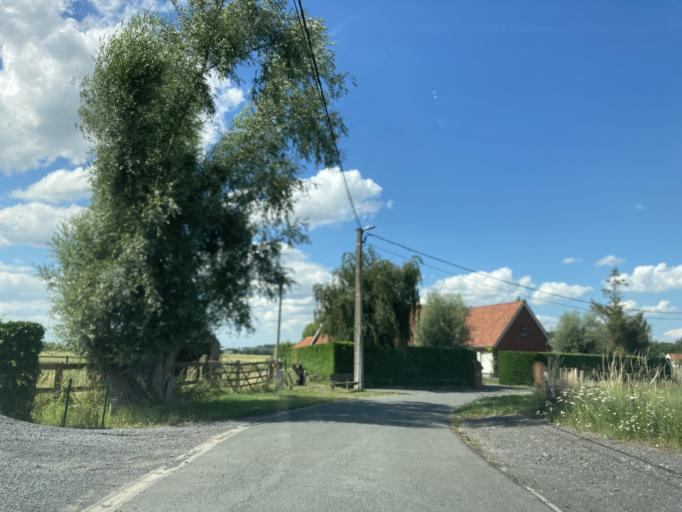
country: BE
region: Flanders
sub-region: Provincie West-Vlaanderen
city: Deerlijk
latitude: 50.8459
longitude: 3.3982
